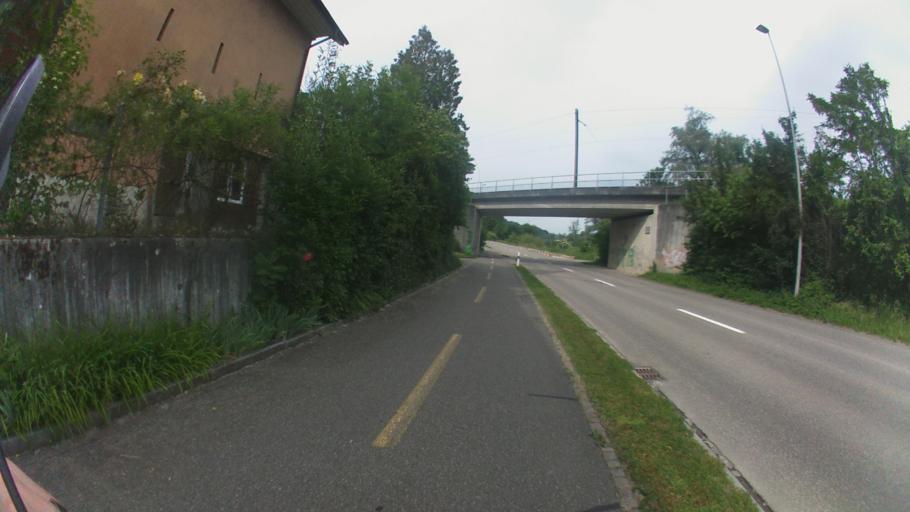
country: CH
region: Aargau
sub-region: Bezirk Zurzach
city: Koblenz
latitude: 47.5988
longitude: 8.2188
